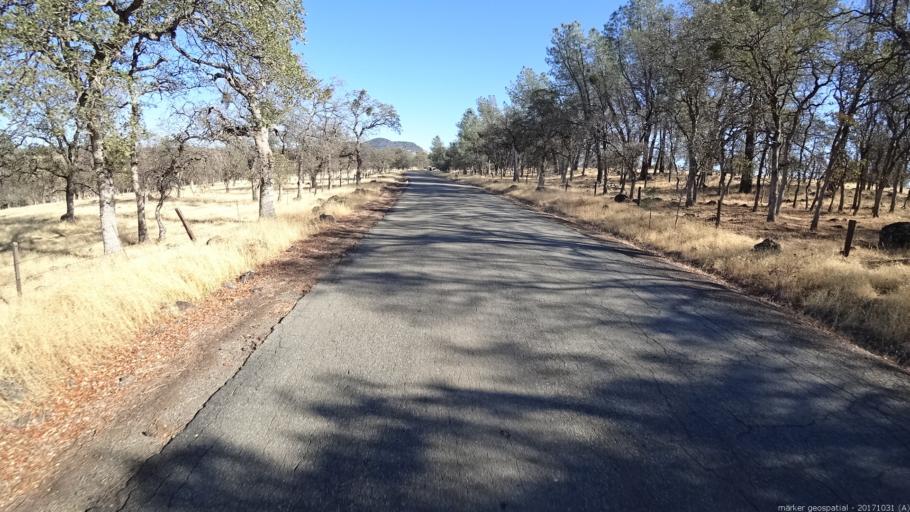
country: US
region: California
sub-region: Shasta County
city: Shingletown
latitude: 40.4583
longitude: -122.0407
